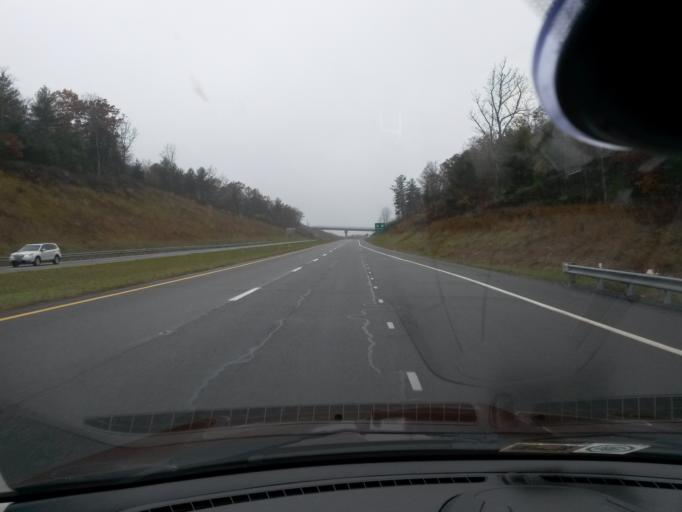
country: US
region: Virginia
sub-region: Carroll County
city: Hillsville
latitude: 36.7445
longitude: -80.7320
